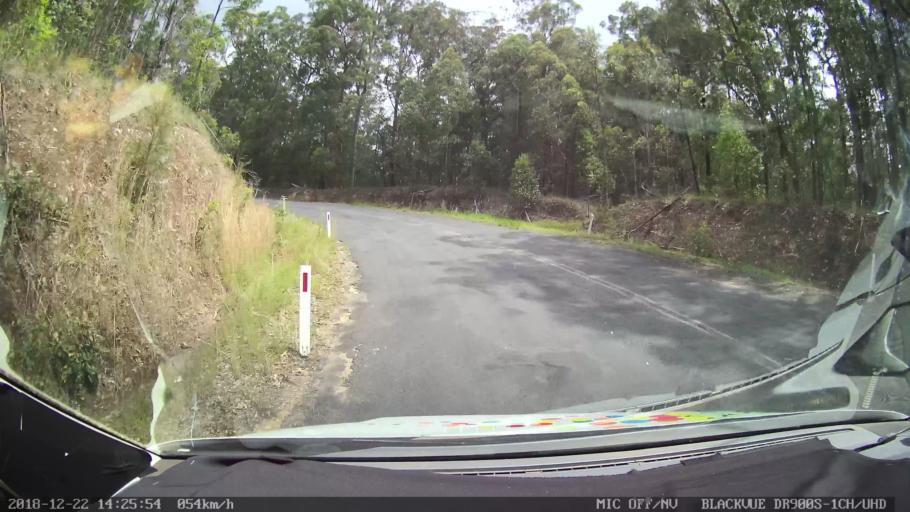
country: AU
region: New South Wales
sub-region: Bellingen
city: Dorrigo
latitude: -30.0546
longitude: 152.6366
